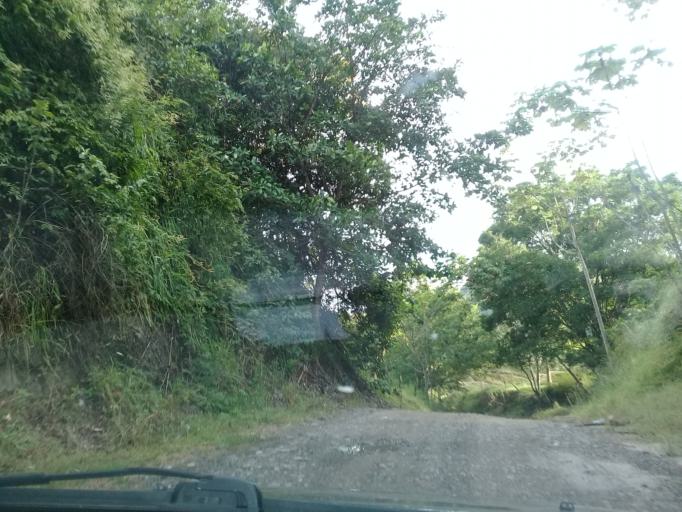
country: CO
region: Antioquia
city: Puerto Triunfo
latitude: 5.7256
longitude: -74.4699
